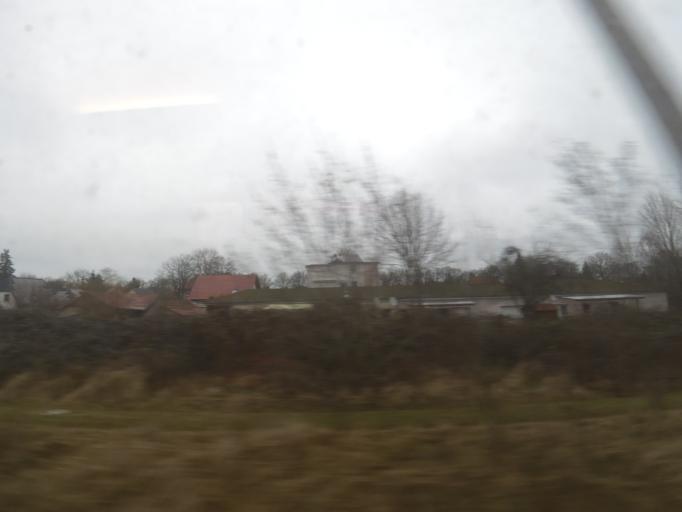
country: DE
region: Brandenburg
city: Falkensee
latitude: 52.5552
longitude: 13.1070
